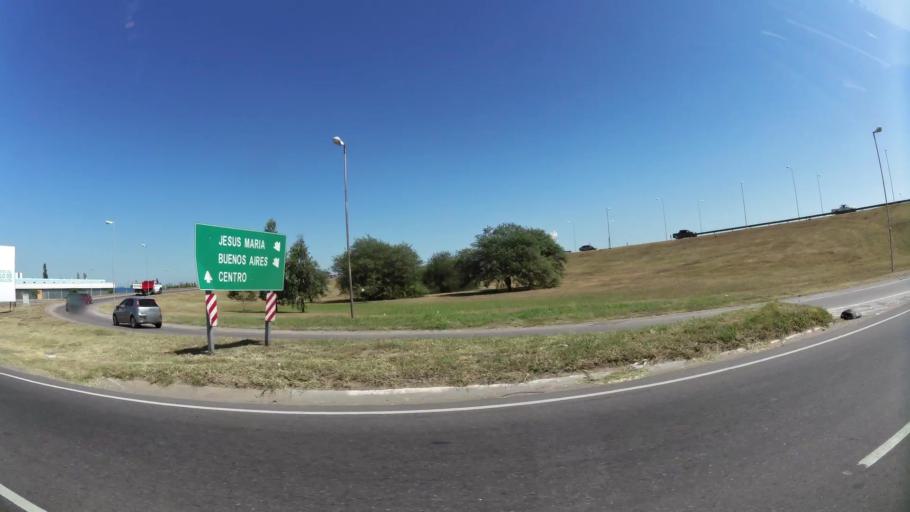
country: AR
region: Cordoba
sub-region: Departamento de Capital
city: Cordoba
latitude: -31.3552
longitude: -64.2030
